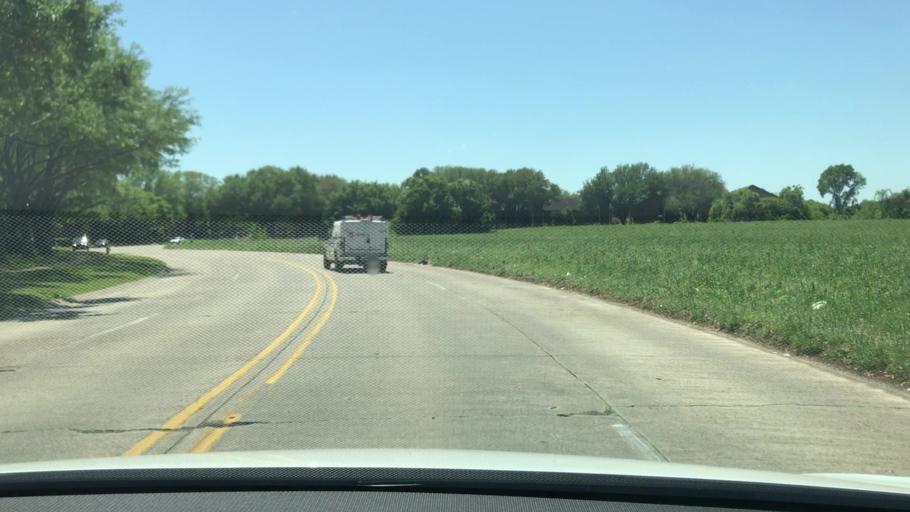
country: US
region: Louisiana
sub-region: Bossier Parish
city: Bossier City
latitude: 32.4261
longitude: -93.7099
